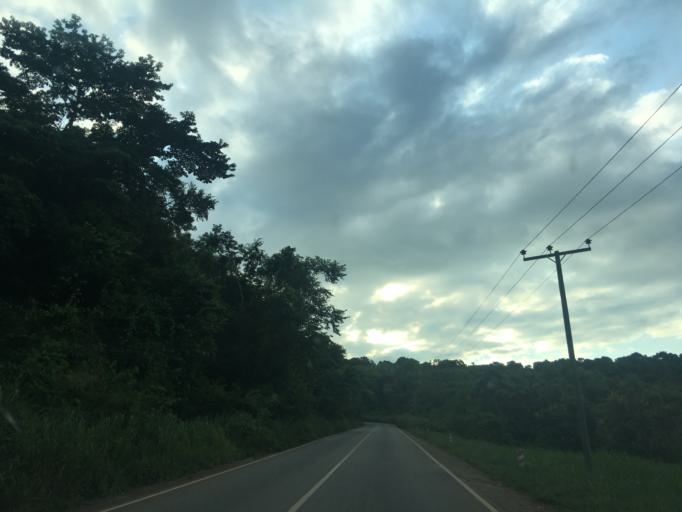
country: GH
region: Western
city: Bibiani
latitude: 6.4644
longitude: -2.3285
